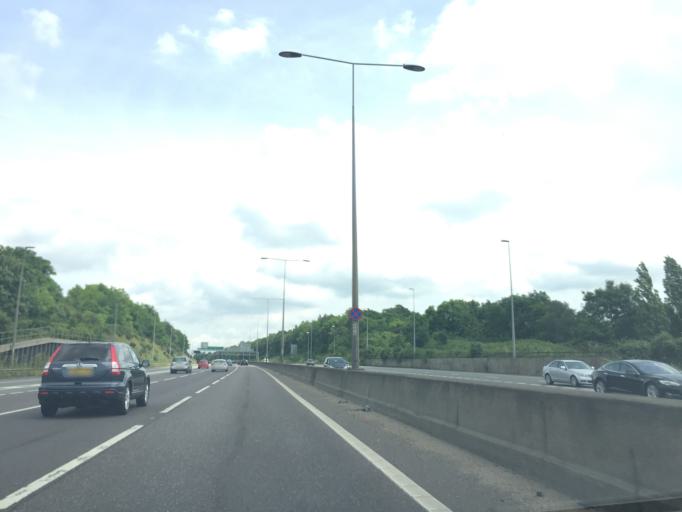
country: GB
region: England
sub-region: Kent
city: Stone
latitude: 51.4275
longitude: 0.2526
